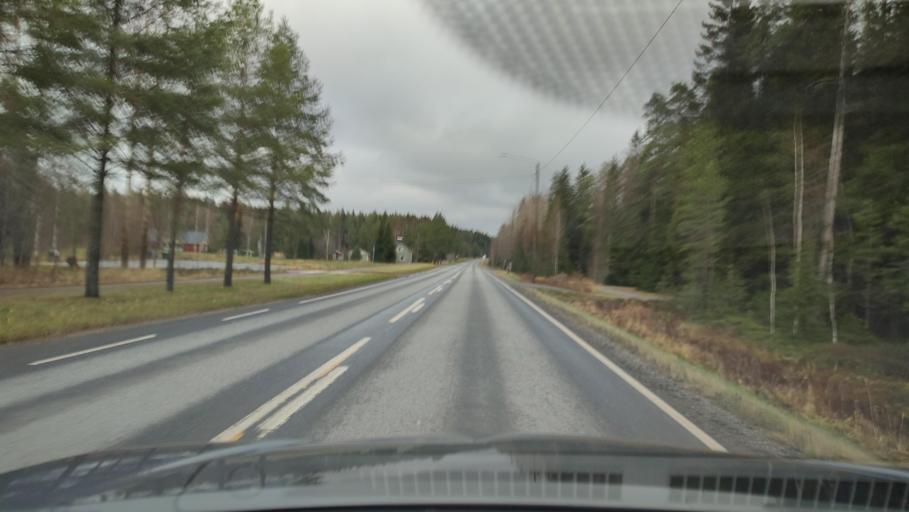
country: FI
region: Southern Ostrobothnia
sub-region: Suupohja
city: Kauhajoki
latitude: 62.3974
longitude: 22.1576
